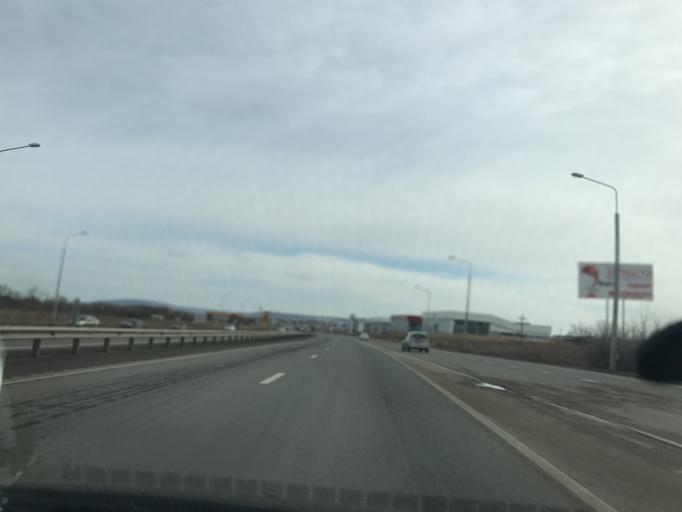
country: RU
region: Stavropol'skiy
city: Andzhiyevskiy
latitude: 44.2089
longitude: 43.0885
